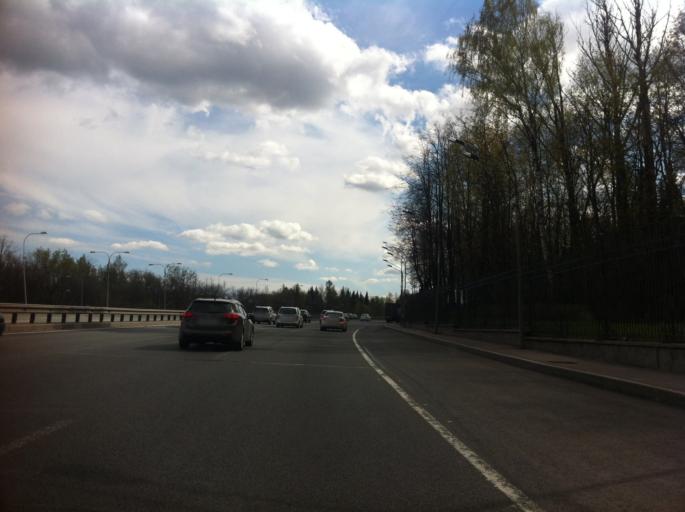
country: RU
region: St.-Petersburg
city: Aleksandrovskaya
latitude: 59.7720
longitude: 30.3321
